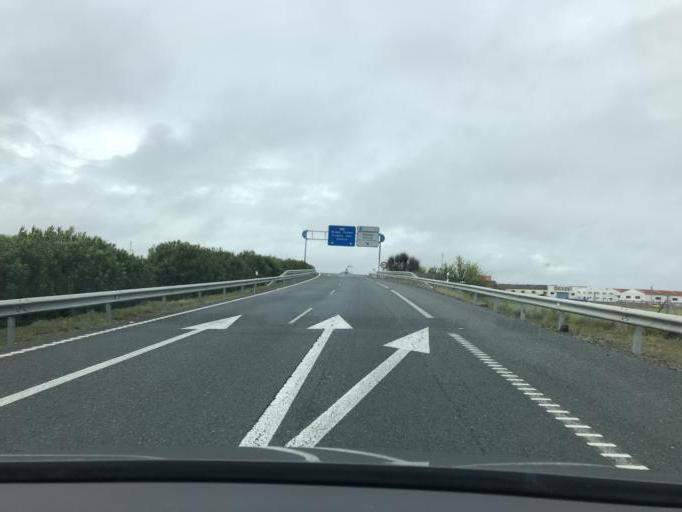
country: ES
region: Andalusia
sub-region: Provincia de Sevilla
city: El Arahal
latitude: 37.2550
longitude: -5.5398
